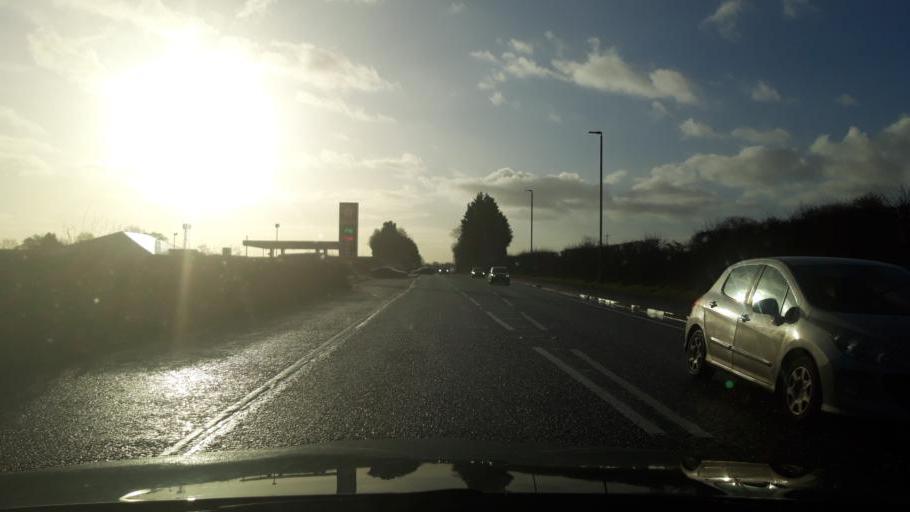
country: GB
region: Northern Ireland
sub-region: Coleraine District
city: Coleraine
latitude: 55.1110
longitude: -6.6905
